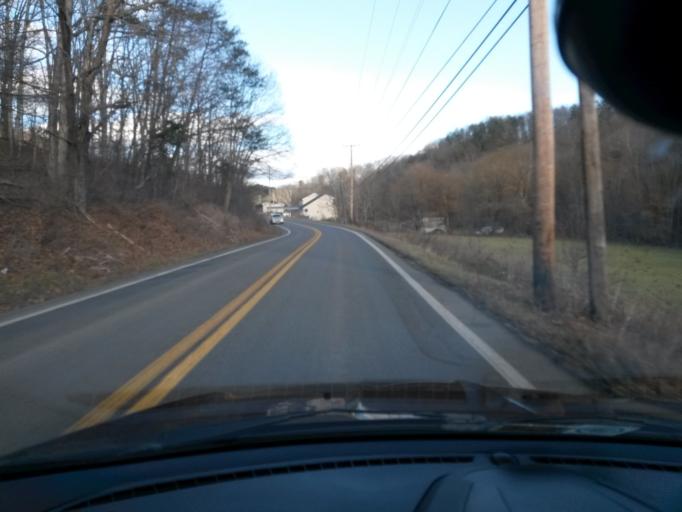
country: US
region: Virginia
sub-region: Giles County
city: Narrows
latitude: 37.3974
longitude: -80.7765
